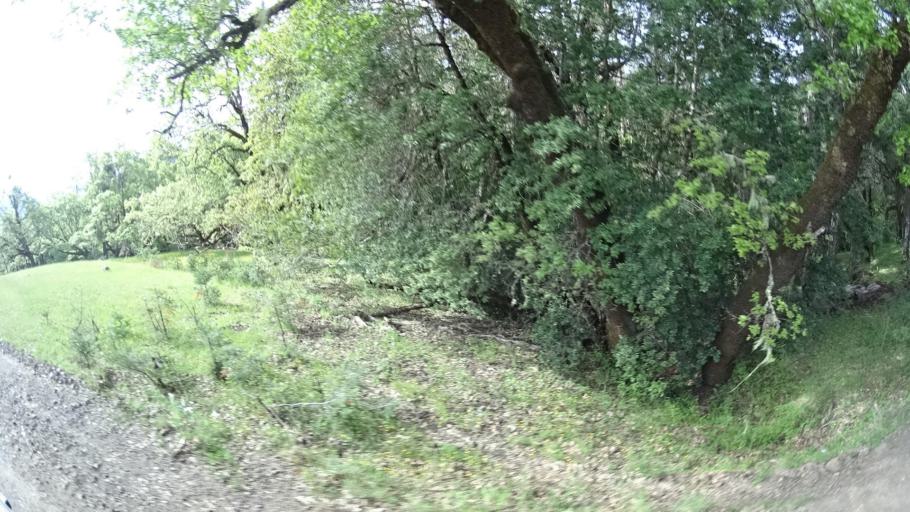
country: US
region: California
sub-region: Humboldt County
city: Redway
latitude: 40.2077
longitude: -123.6886
